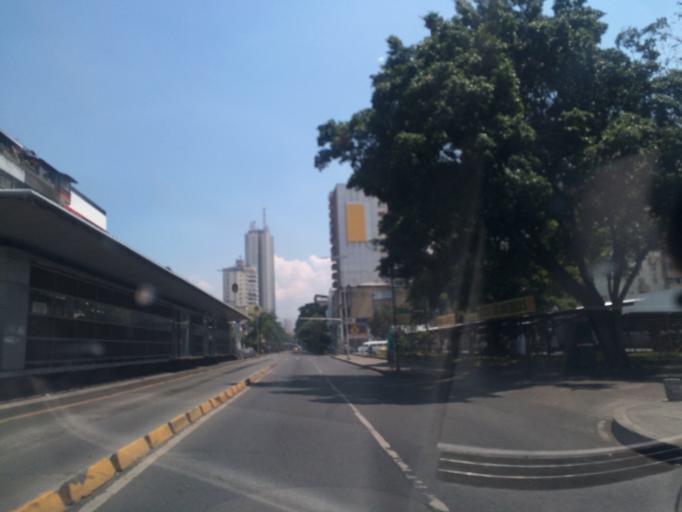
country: CO
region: Valle del Cauca
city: Cali
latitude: 3.4640
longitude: -76.5251
